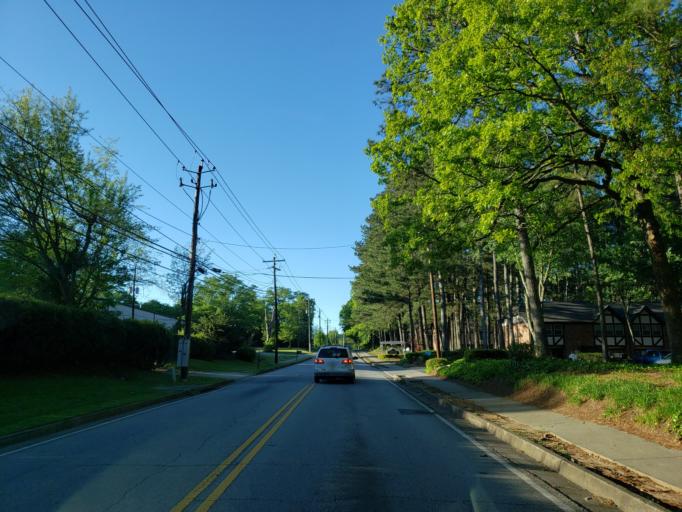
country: US
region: Georgia
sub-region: Cobb County
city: Fair Oaks
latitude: 33.9056
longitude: -84.5400
